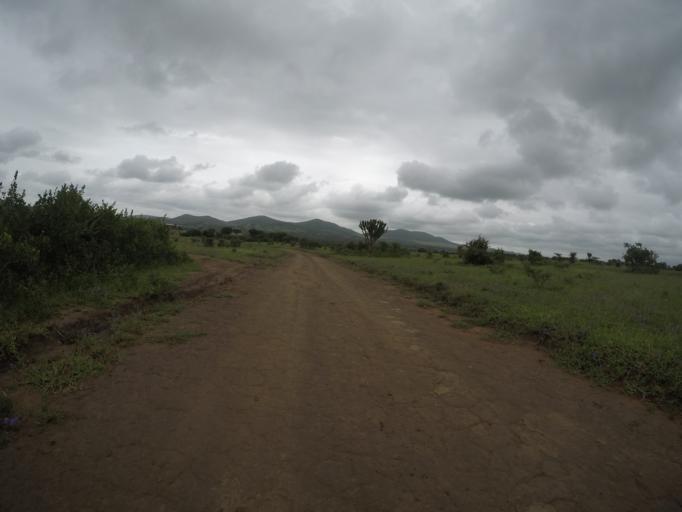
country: ZA
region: KwaZulu-Natal
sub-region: uThungulu District Municipality
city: Empangeni
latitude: -28.6043
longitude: 31.8644
